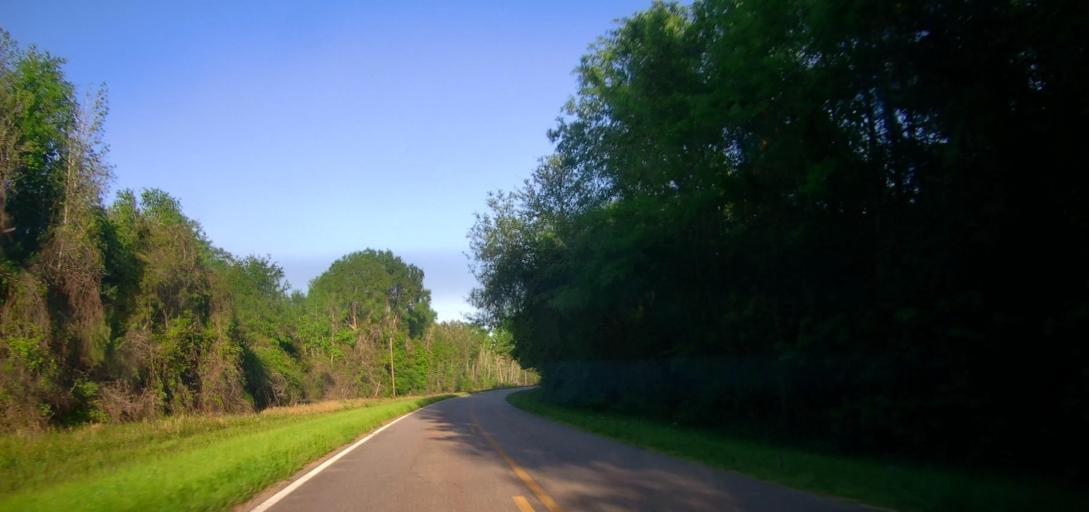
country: US
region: Georgia
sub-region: Macon County
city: Oglethorpe
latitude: 32.3048
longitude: -84.1072
